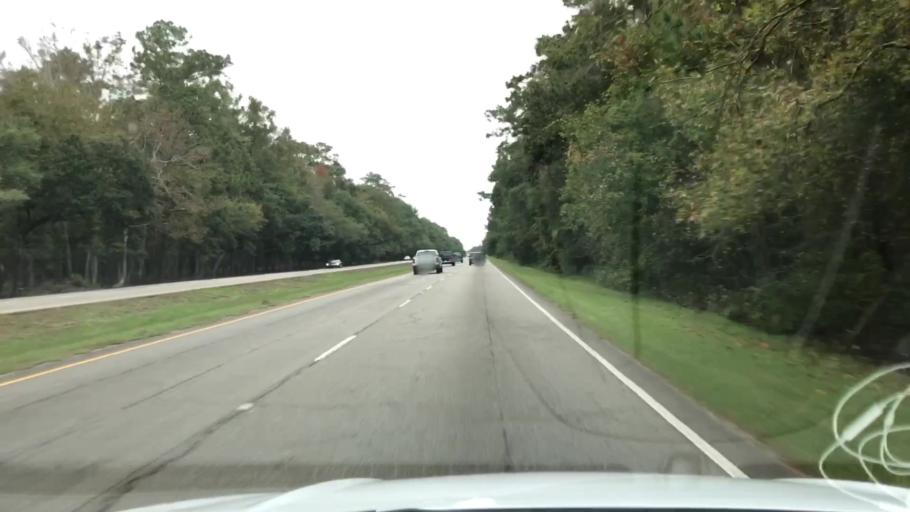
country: US
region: South Carolina
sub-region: Georgetown County
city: Murrells Inlet
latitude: 33.5164
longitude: -79.0713
